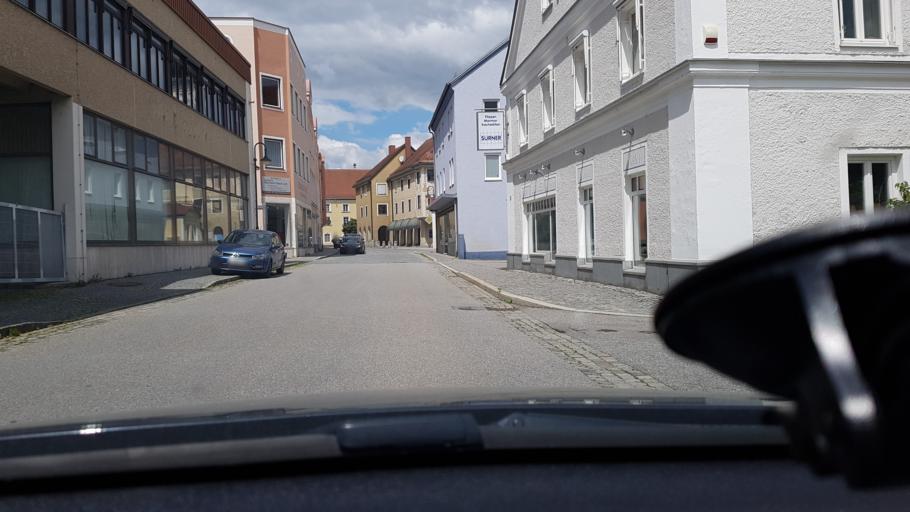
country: DE
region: Bavaria
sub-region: Lower Bavaria
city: Rotthalmunster
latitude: 48.3592
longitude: 13.2045
